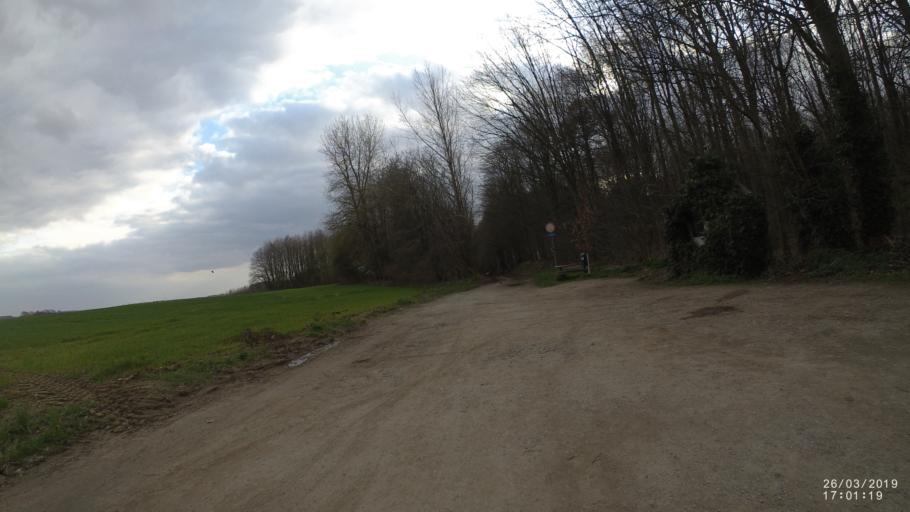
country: BE
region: Flanders
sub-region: Provincie Vlaams-Brabant
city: Bertem
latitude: 50.8342
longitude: 4.6008
